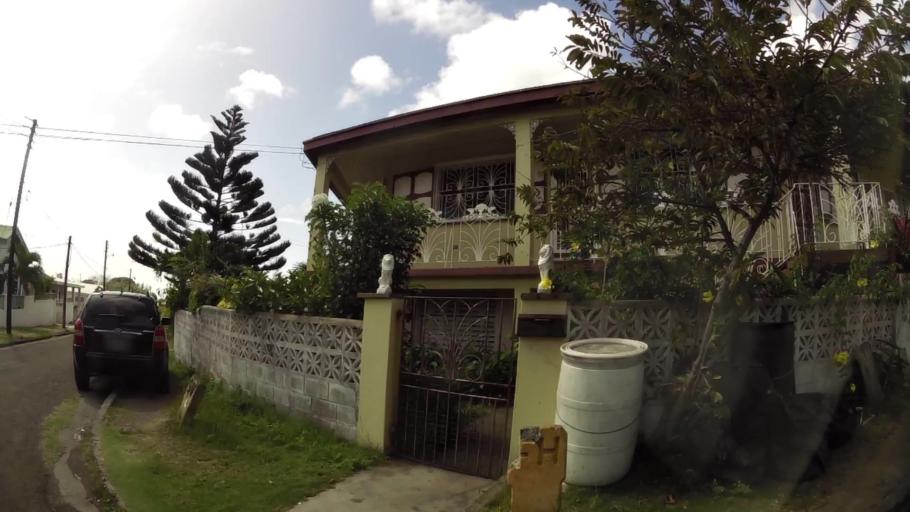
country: KN
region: Saint George Basseterre
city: Basseterre
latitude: 17.3005
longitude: -62.7270
